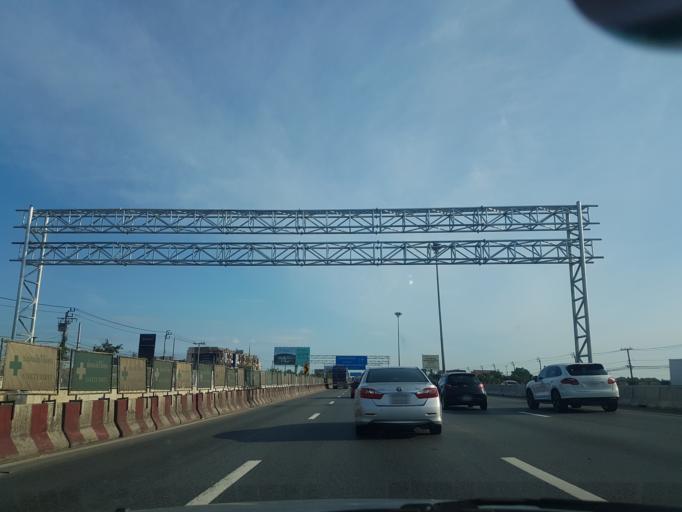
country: TH
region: Bangkok
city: Saphan Sung
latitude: 13.7655
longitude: 100.6940
